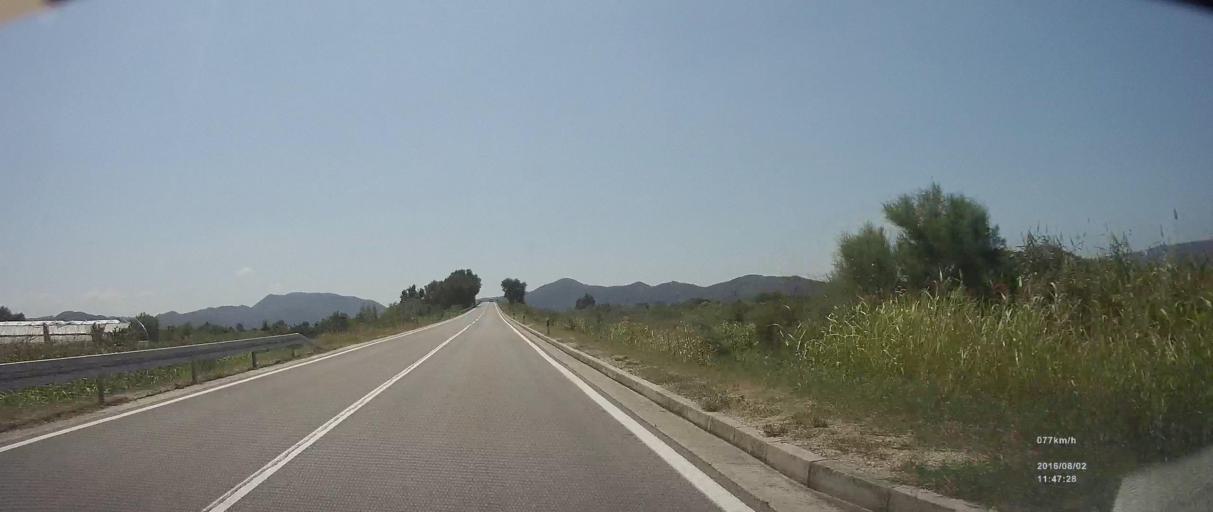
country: HR
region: Dubrovacko-Neretvanska
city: Komin
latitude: 43.0437
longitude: 17.4822
